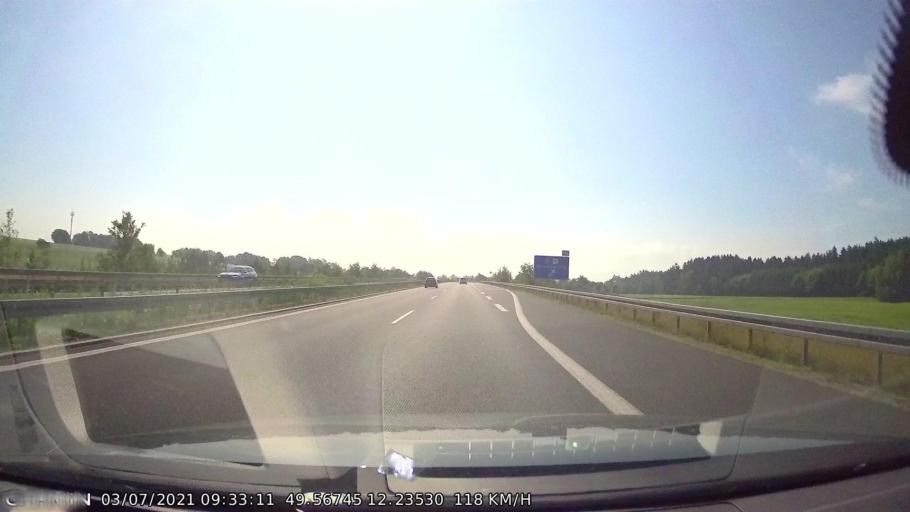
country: DE
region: Bavaria
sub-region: Upper Palatinate
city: Leuchtenberg
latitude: 49.5673
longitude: 12.2353
